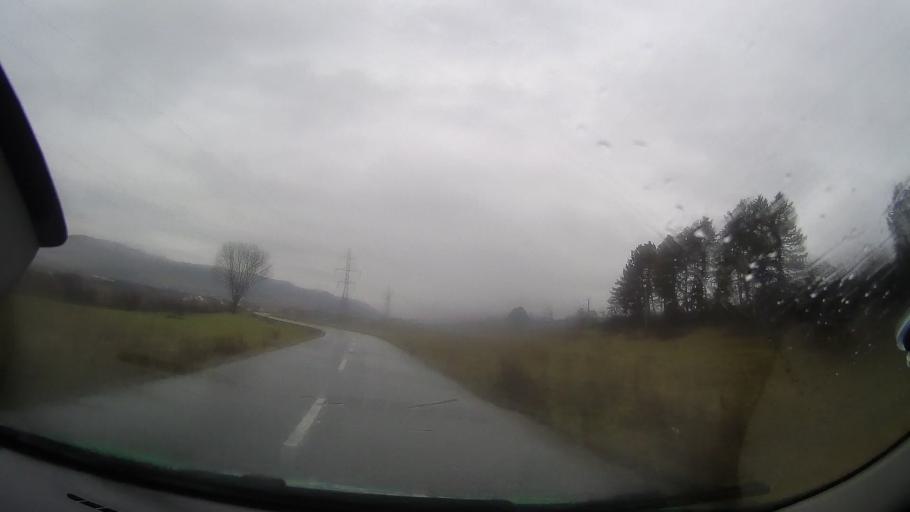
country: RO
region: Bistrita-Nasaud
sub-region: Comuna Mariselu
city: Mariselu
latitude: 47.0290
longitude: 24.4938
